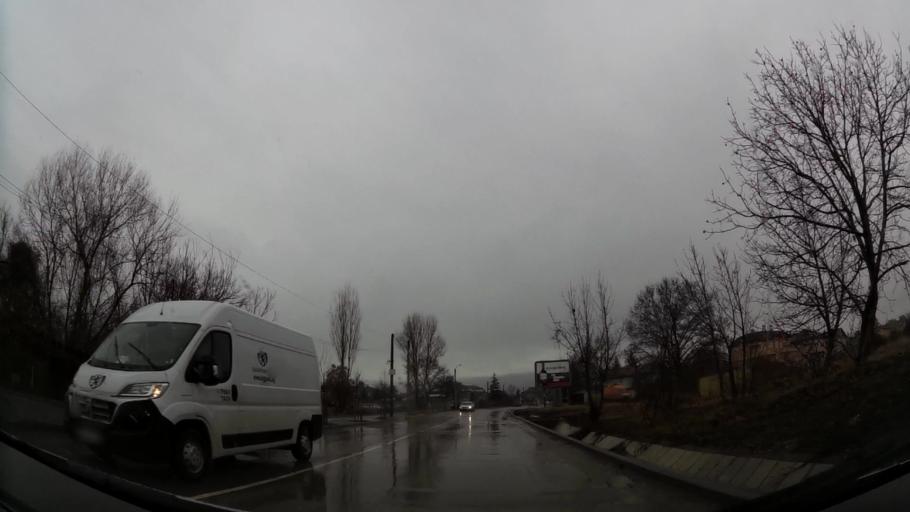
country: BG
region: Sofia-Capital
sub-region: Stolichna Obshtina
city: Sofia
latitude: 42.6354
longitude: 23.4084
